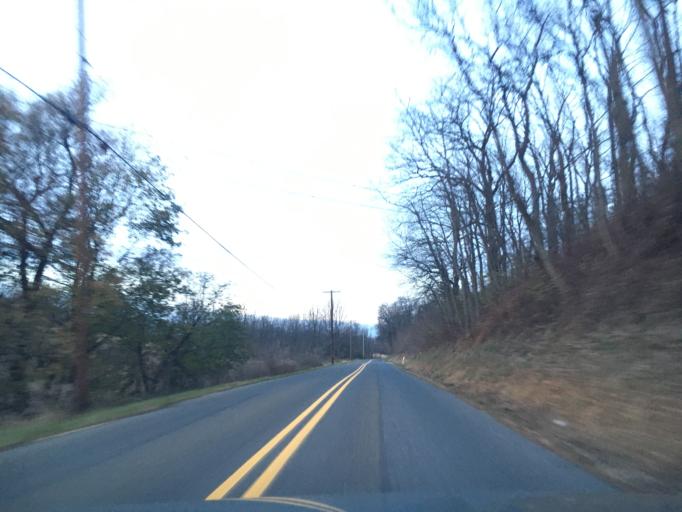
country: US
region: Pennsylvania
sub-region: Lehigh County
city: Schnecksville
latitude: 40.6818
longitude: -75.5745
